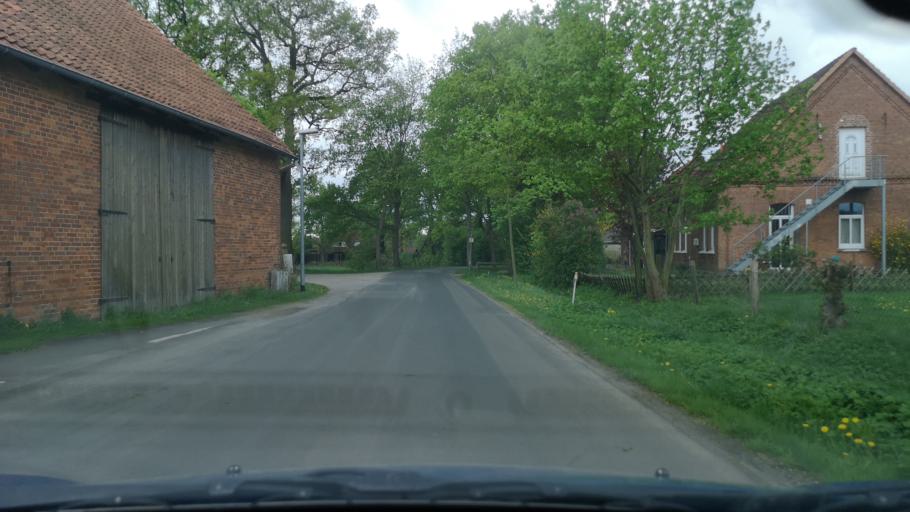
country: DE
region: Lower Saxony
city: Langenhagen
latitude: 52.4857
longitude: 9.7654
